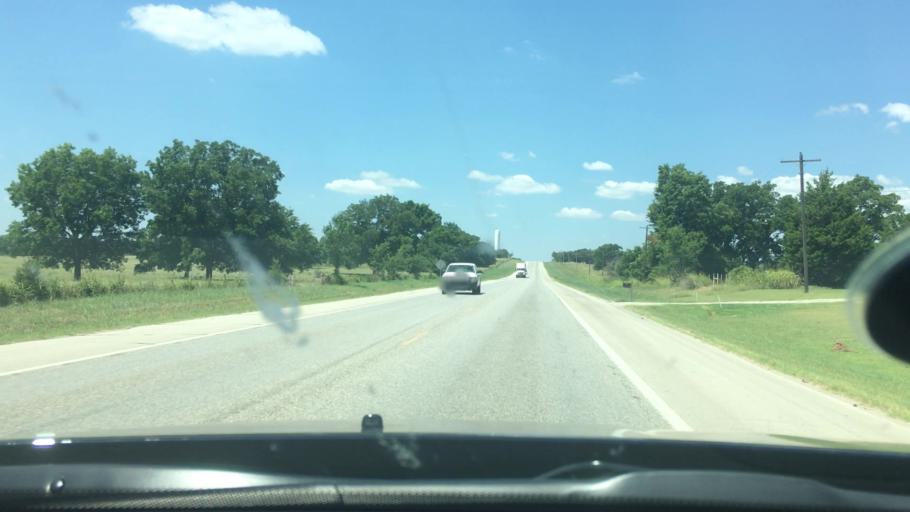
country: US
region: Oklahoma
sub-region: Carter County
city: Dickson
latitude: 34.1872
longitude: -96.8995
